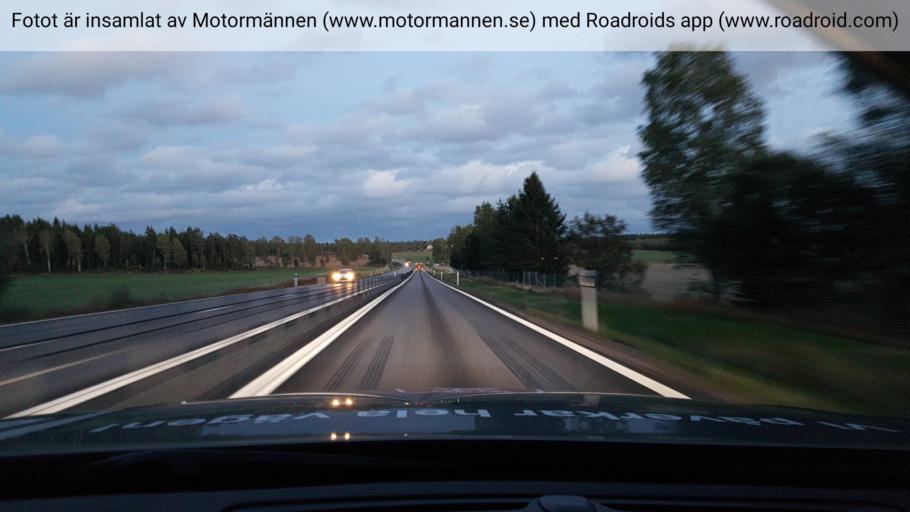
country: SE
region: Vaermland
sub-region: Karlstads Kommun
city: Skattkarr
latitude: 59.3980
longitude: 13.8036
